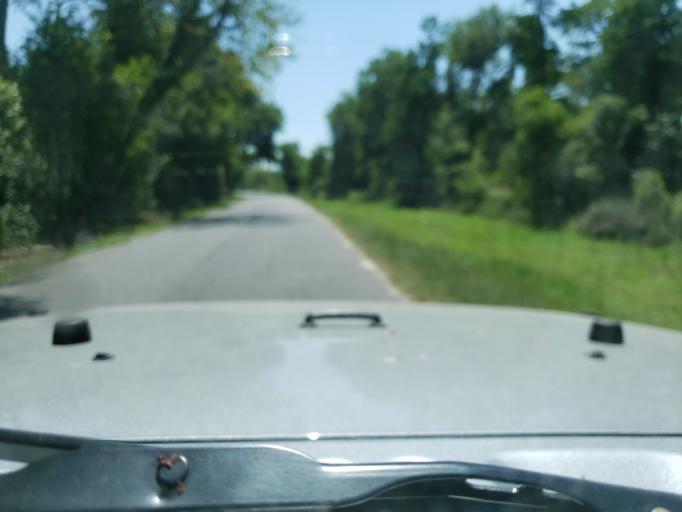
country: US
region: Georgia
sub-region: Chatham County
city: Thunderbolt
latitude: 32.0794
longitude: -81.0402
